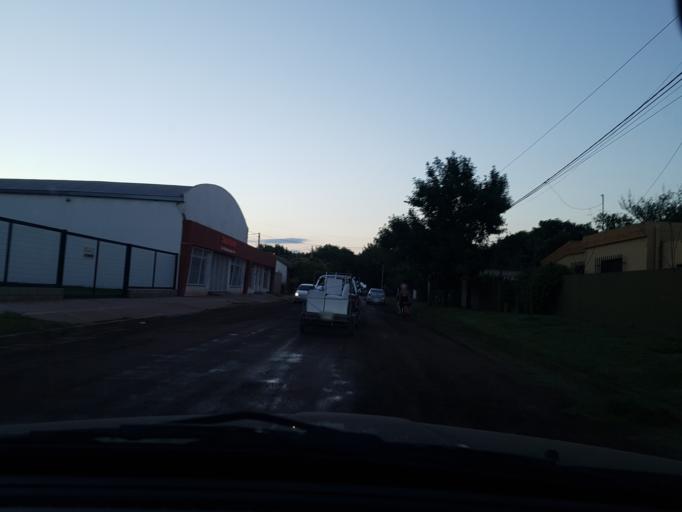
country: AR
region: Cordoba
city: General Cabrera
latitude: -32.7610
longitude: -63.7974
